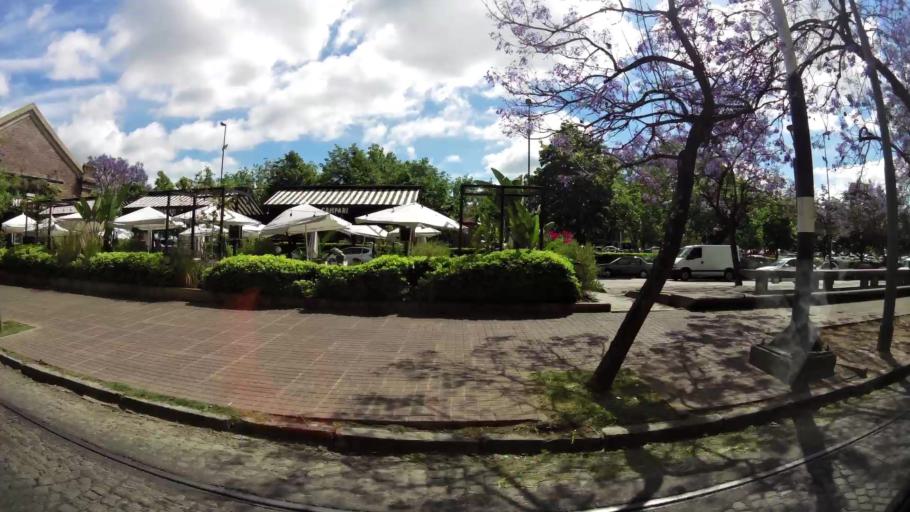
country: AR
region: Santa Fe
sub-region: Departamento de Rosario
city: Rosario
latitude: -32.9353
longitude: -60.6436
